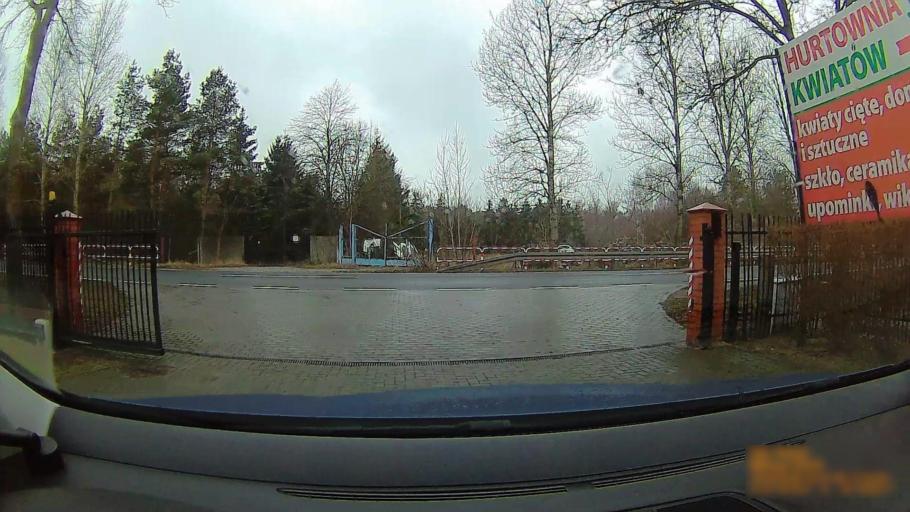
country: PL
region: Greater Poland Voivodeship
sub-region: Konin
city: Konin
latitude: 52.1721
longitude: 18.2735
